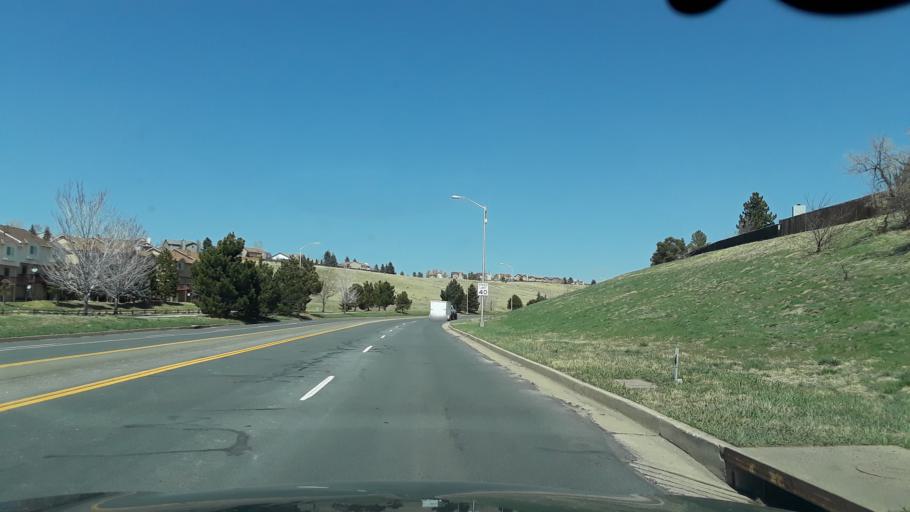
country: US
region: Colorado
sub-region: El Paso County
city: Black Forest
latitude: 38.9462
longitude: -104.7426
